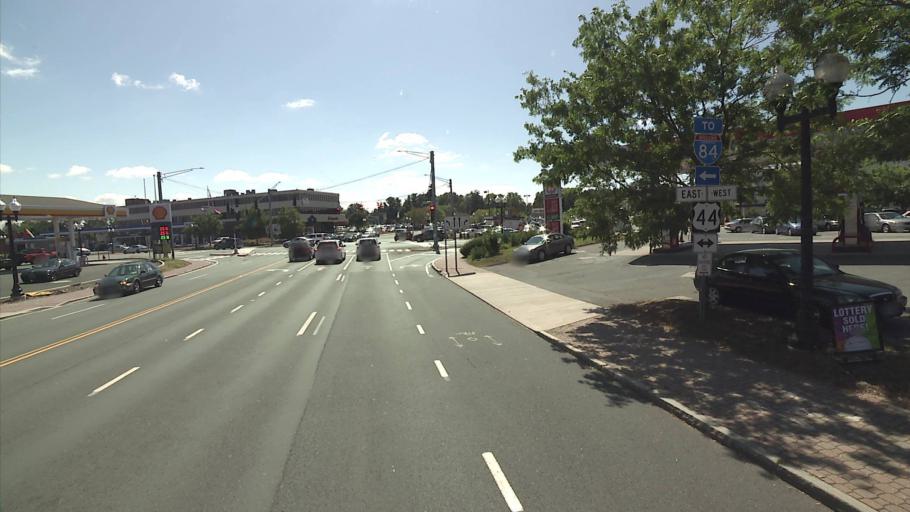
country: US
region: Connecticut
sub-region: Hartford County
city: West Hartford
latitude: 41.7862
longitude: -72.7475
